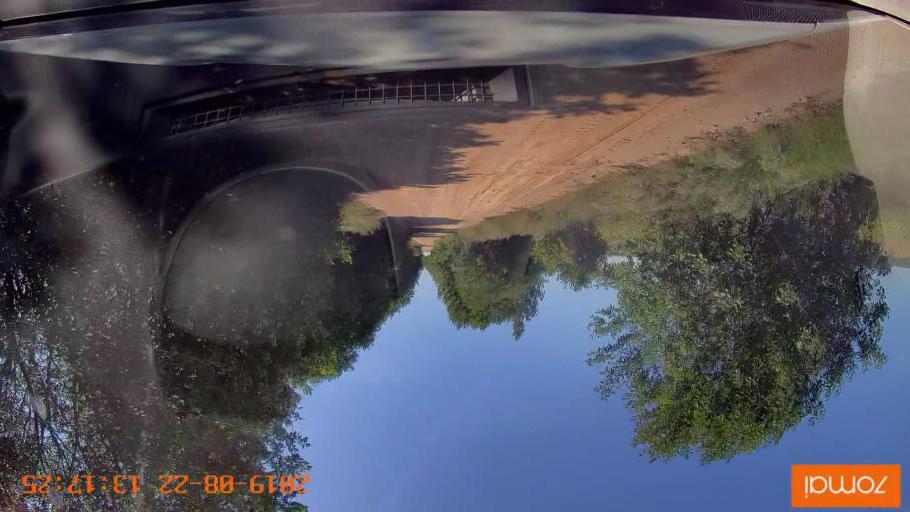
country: BY
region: Minsk
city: Prawdzinski
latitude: 53.2482
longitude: 27.9220
